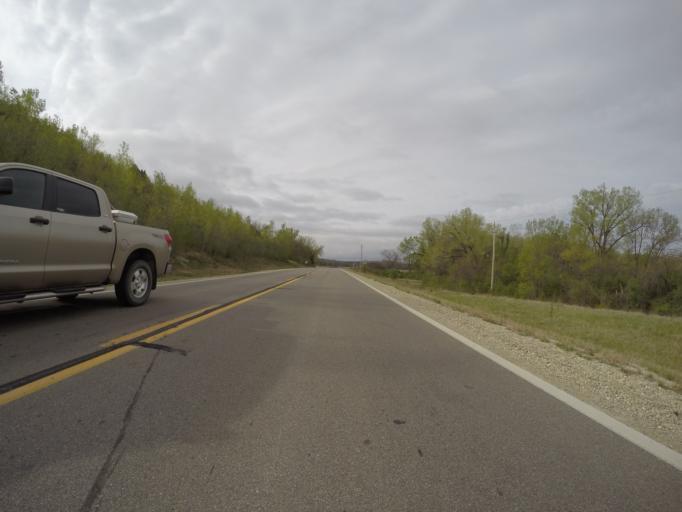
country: US
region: Kansas
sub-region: Riley County
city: Manhattan
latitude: 39.1422
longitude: -96.5586
